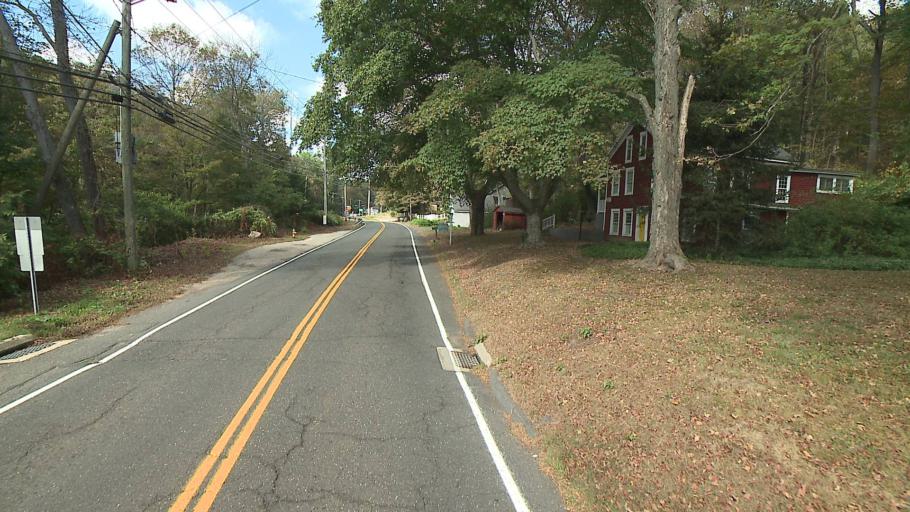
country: US
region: Connecticut
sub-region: New Haven County
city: Oxford
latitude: 41.4323
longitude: -73.1116
